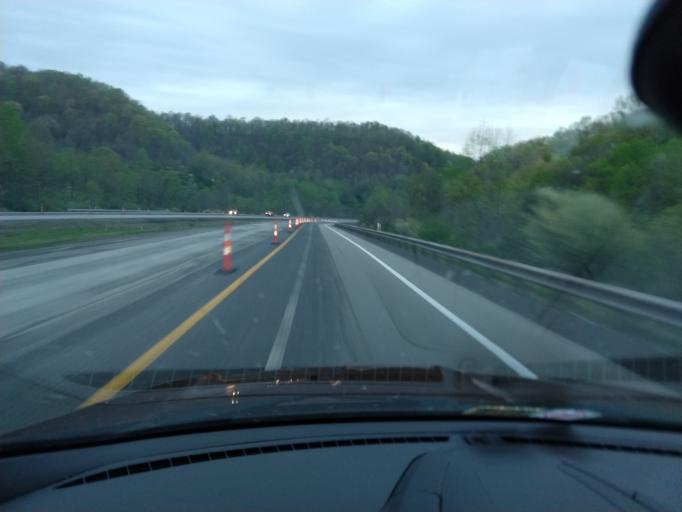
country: US
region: West Virginia
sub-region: Braxton County
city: Sutton
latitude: 38.7234
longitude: -80.6673
